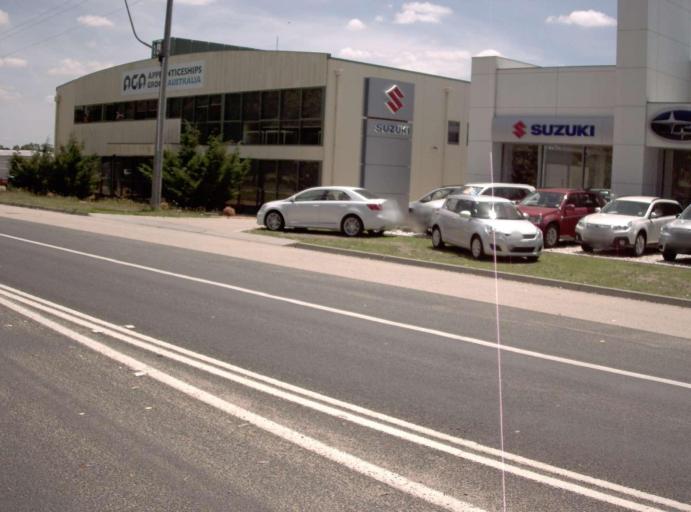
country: AU
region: Victoria
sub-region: East Gippsland
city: Bairnsdale
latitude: -37.8389
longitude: 147.5947
